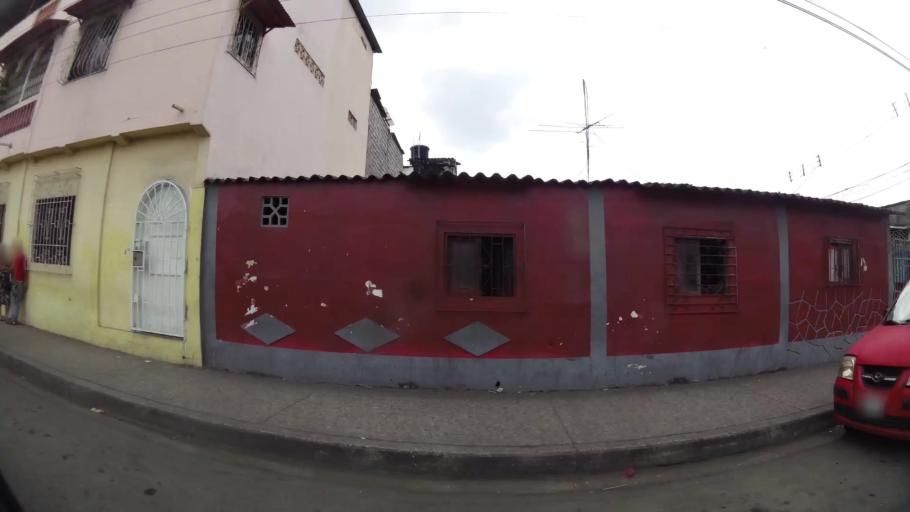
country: EC
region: Guayas
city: Guayaquil
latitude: -2.2295
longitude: -79.9050
